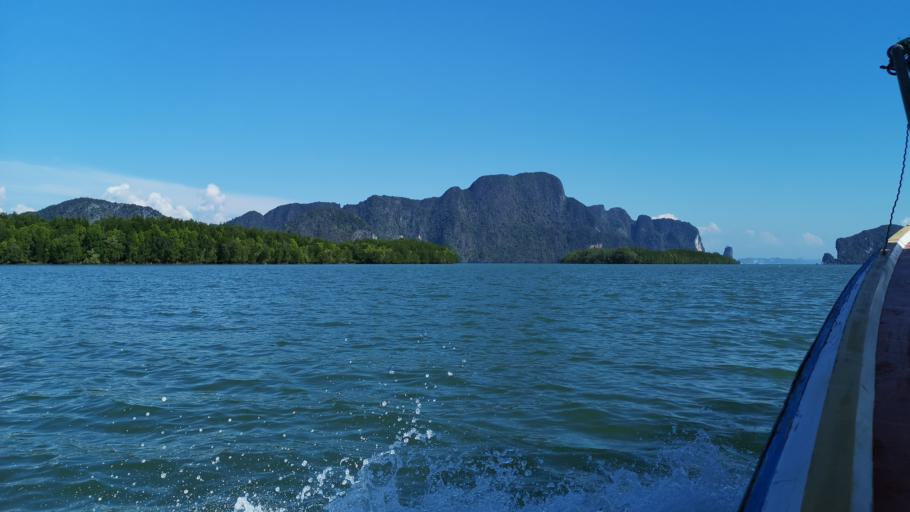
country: TH
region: Phangnga
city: Takua Thung
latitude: 8.2968
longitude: 98.4588
